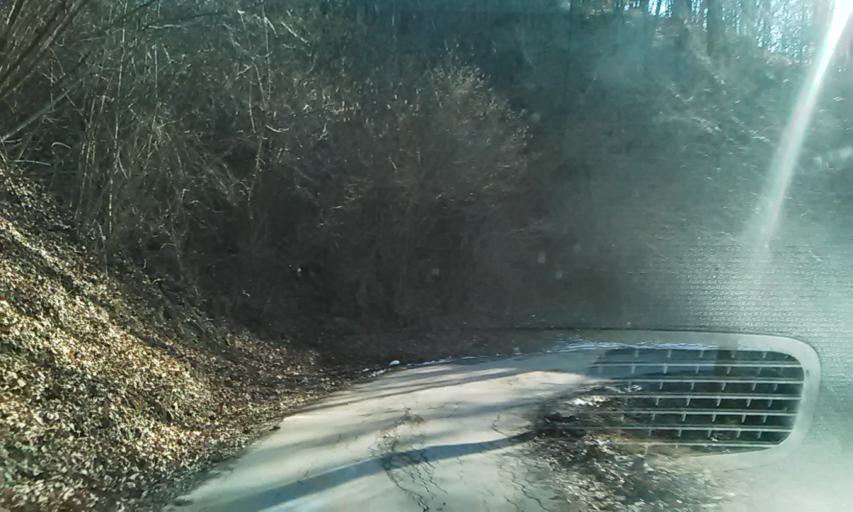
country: IT
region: Piedmont
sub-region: Provincia di Vercelli
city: Valduggia
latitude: 45.7245
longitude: 8.3152
